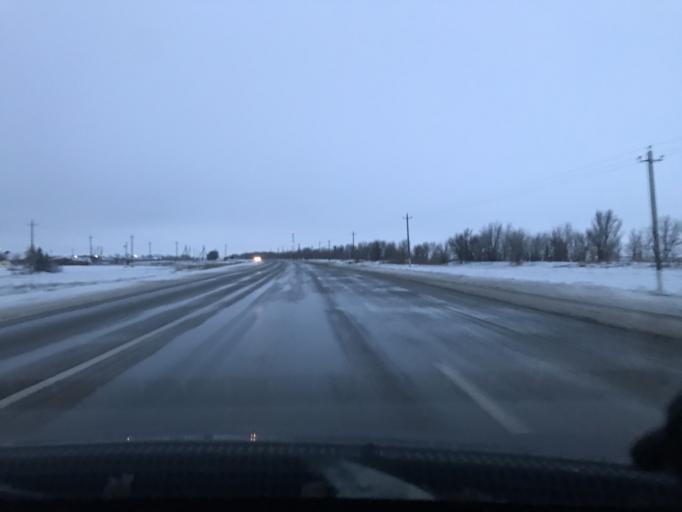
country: RU
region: Rostov
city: Letnik
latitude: 45.9157
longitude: 41.2905
